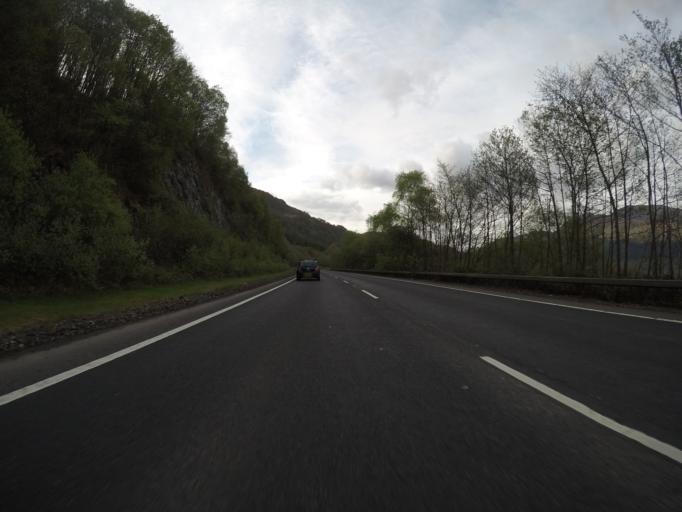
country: GB
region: Scotland
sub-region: Argyll and Bute
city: Helensburgh
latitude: 56.1512
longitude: -4.6666
